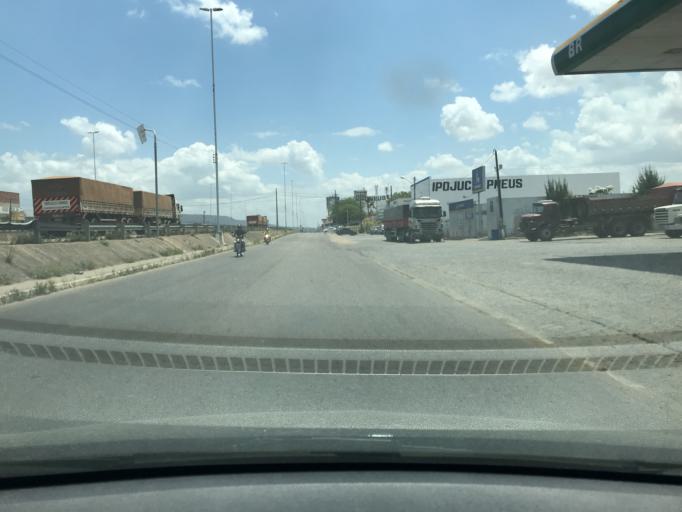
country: BR
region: Pernambuco
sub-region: Bezerros
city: Bezerros
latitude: -8.2395
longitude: -35.7477
